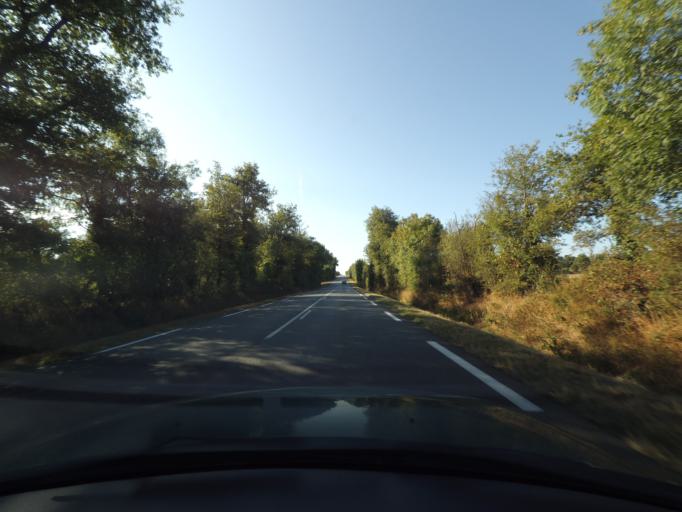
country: FR
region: Poitou-Charentes
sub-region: Departement des Deux-Sevres
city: Viennay
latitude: 46.7038
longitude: -0.2832
